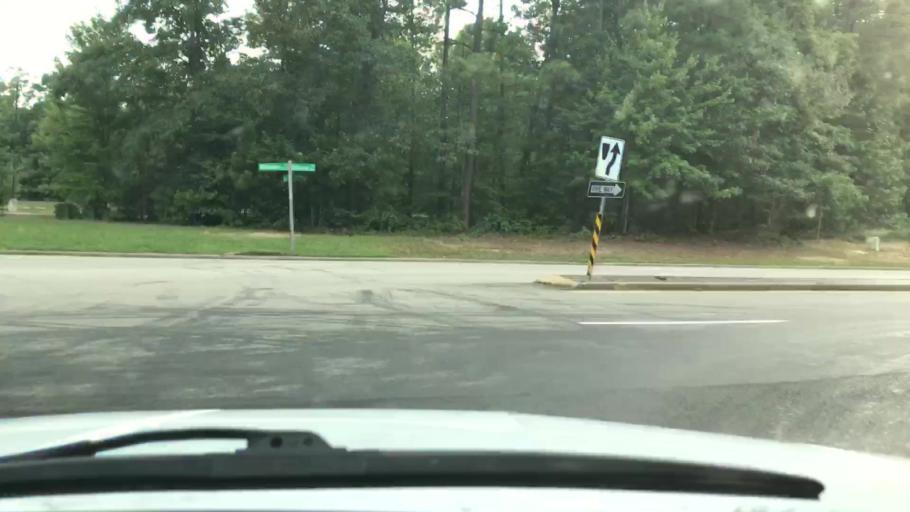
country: US
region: Virginia
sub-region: Chesterfield County
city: Chesterfield
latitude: 37.4109
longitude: -77.5540
